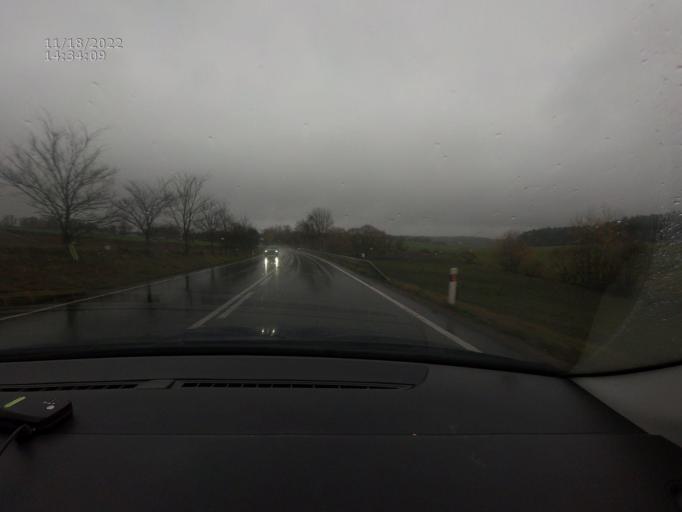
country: CZ
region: Jihocesky
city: Milevsko
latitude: 49.4542
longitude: 14.3159
